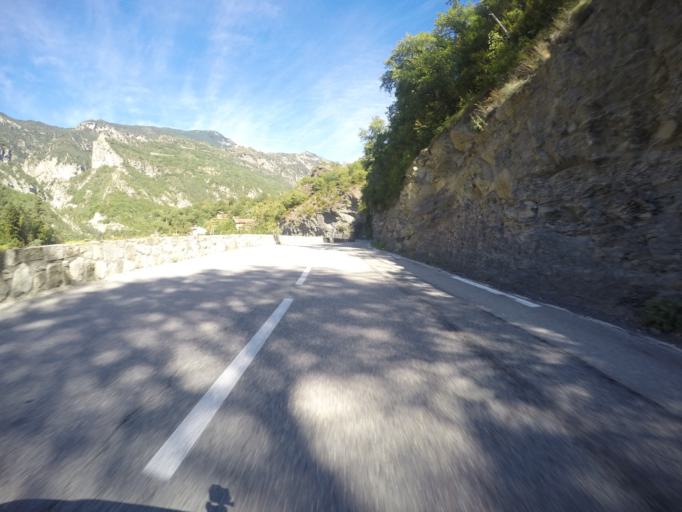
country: FR
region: Provence-Alpes-Cote d'Azur
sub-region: Departement des Alpes-Maritimes
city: Gilette
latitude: 43.9716
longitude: 7.1470
